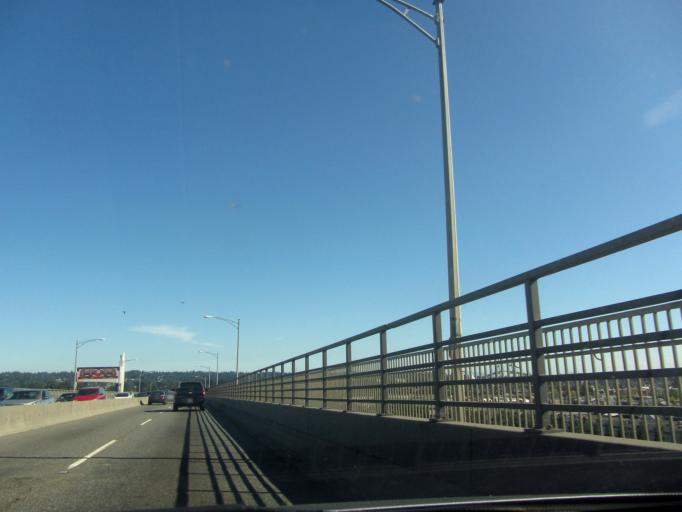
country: CA
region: British Columbia
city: New Westminster
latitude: 49.1964
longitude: -122.9473
